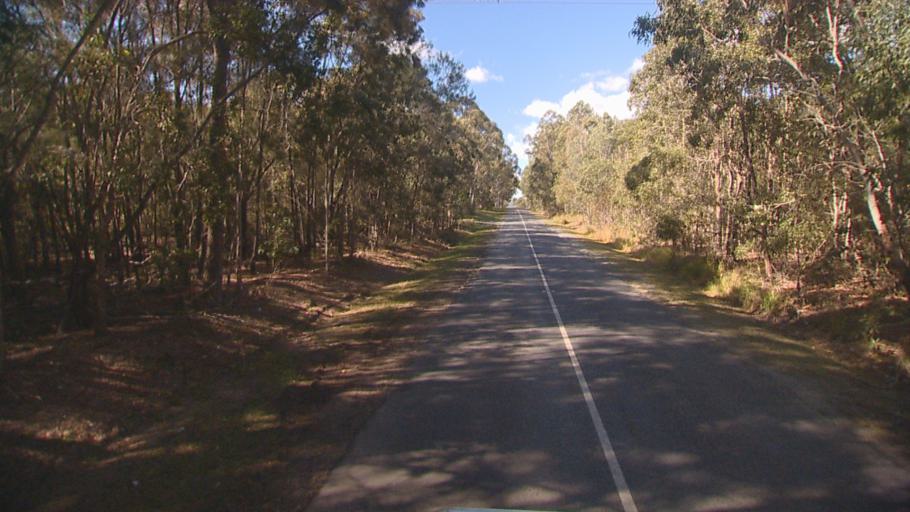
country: AU
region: Queensland
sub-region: Logan
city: Chambers Flat
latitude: -27.7919
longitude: 153.0781
